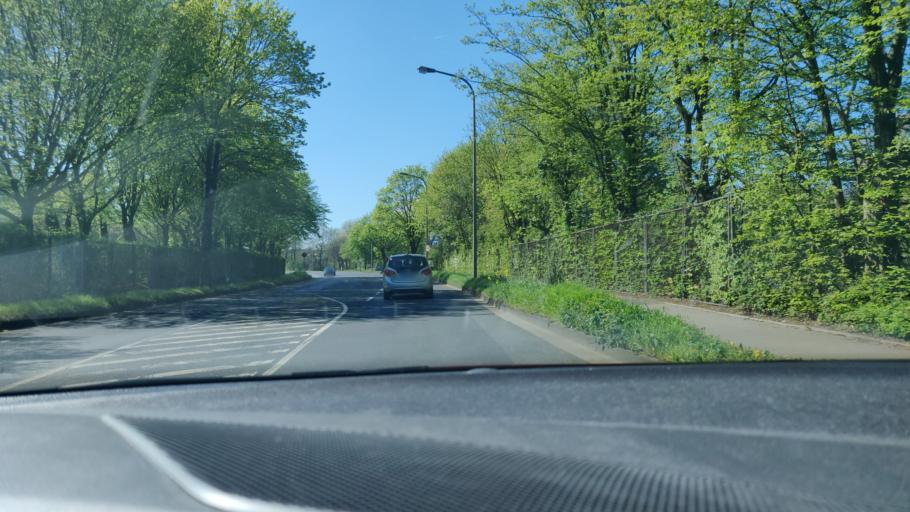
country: DE
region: North Rhine-Westphalia
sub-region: Regierungsbezirk Dusseldorf
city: Mettmann
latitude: 51.2461
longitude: 6.9846
